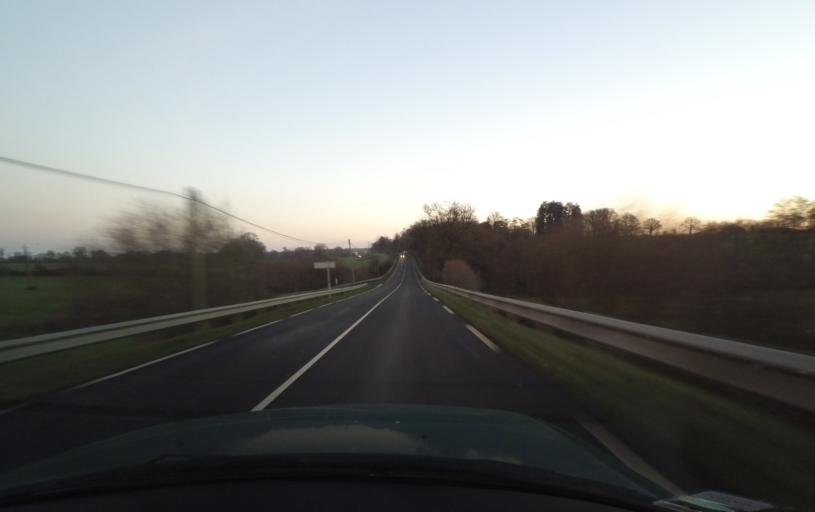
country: FR
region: Pays de la Loire
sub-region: Departement de la Mayenne
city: Soulge-sur-Ouette
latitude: 48.0932
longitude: -0.5266
